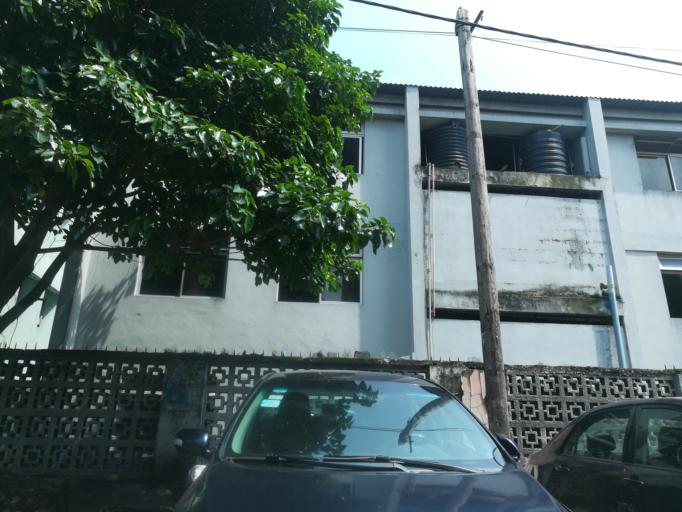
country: NG
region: Lagos
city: Lagos
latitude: 6.4510
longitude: 3.3926
